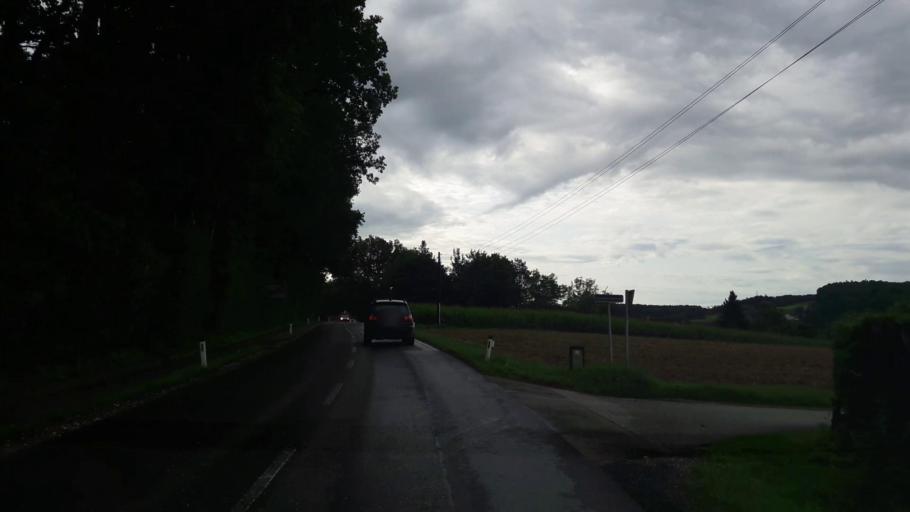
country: AT
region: Styria
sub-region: Politischer Bezirk Hartberg-Fuerstenfeld
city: Kaindorf
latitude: 47.2187
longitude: 15.9140
